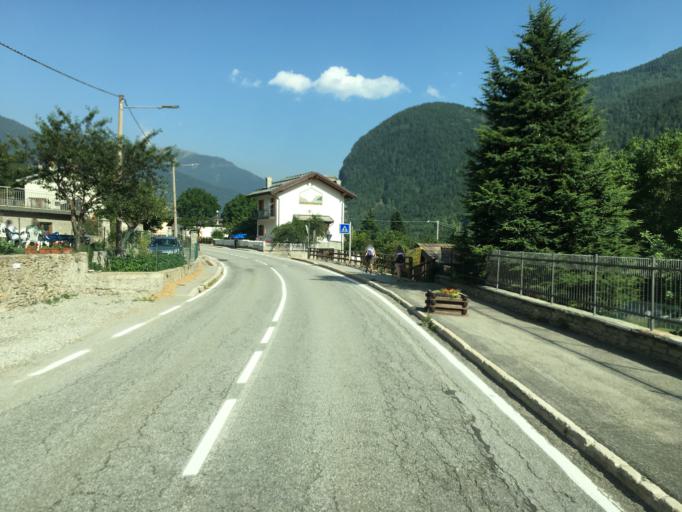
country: IT
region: Piedmont
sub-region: Provincia di Torino
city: Fenestrelle
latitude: 45.0241
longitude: 7.0874
